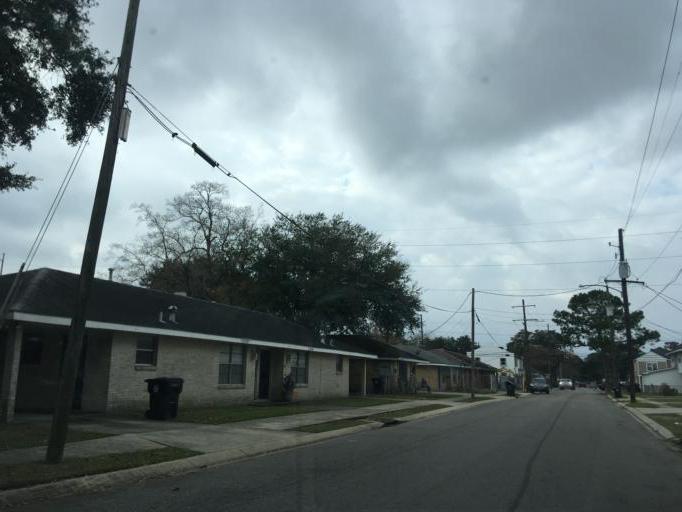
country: US
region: Louisiana
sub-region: Orleans Parish
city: New Orleans
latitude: 29.9950
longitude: -90.0591
